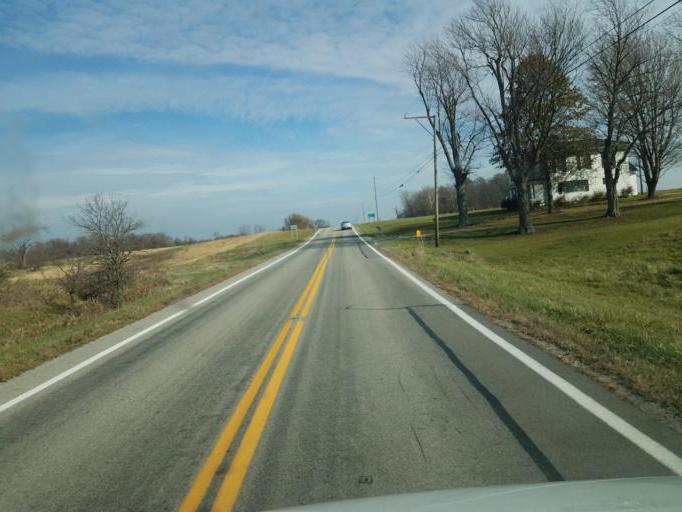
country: US
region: Ohio
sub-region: Hardin County
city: Forest
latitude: 40.7018
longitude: -83.4592
